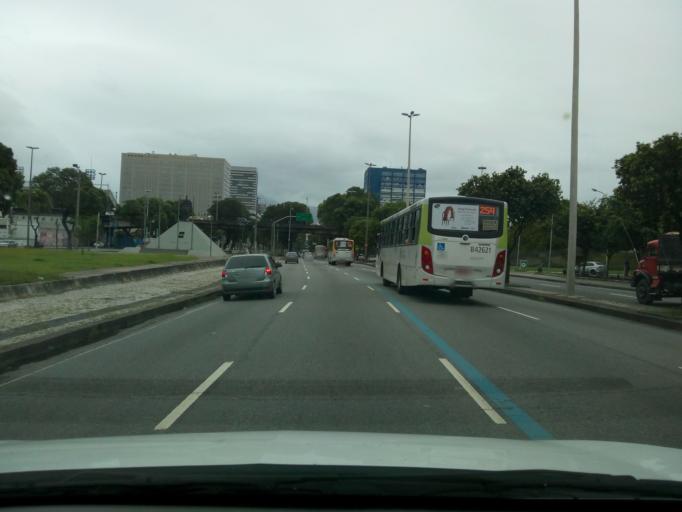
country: BR
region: Rio de Janeiro
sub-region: Rio De Janeiro
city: Rio de Janeiro
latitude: -22.9065
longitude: -43.1959
